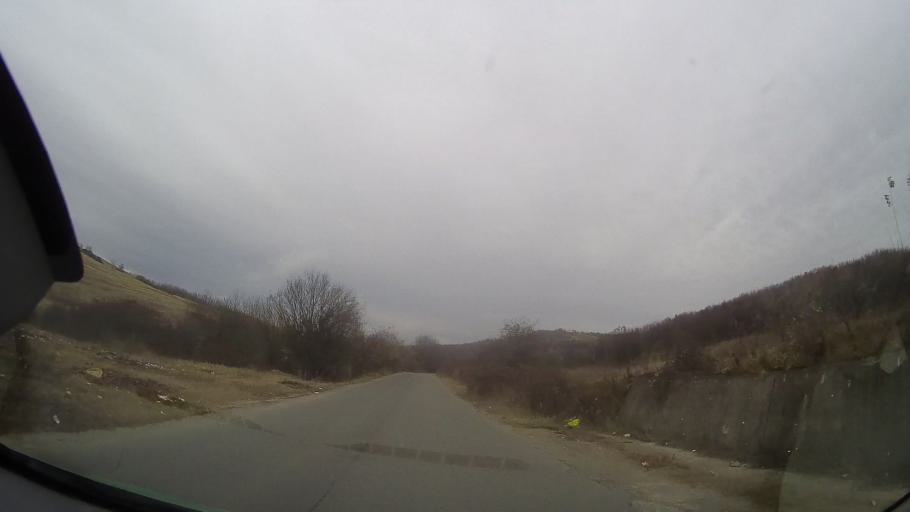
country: RO
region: Prahova
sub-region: Comuna Gornet-Cricov
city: Gornet-Cricov
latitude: 45.0594
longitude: 26.2729
